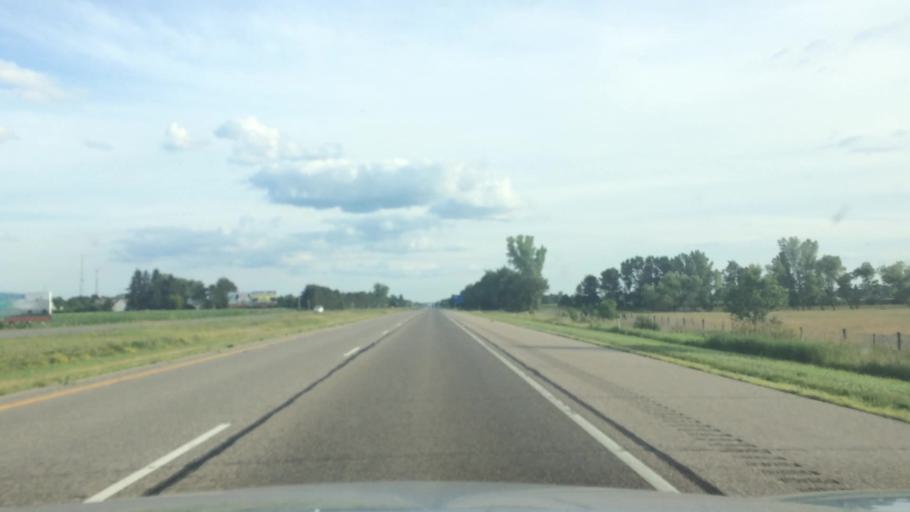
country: US
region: Wisconsin
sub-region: Portage County
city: Plover
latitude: 44.3225
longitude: -89.5236
